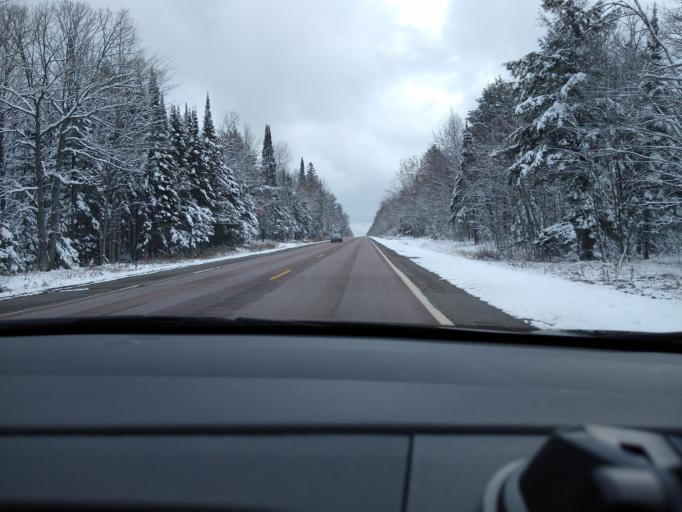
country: US
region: Wisconsin
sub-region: Vilas County
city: Eagle River
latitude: 46.2073
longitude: -89.0277
